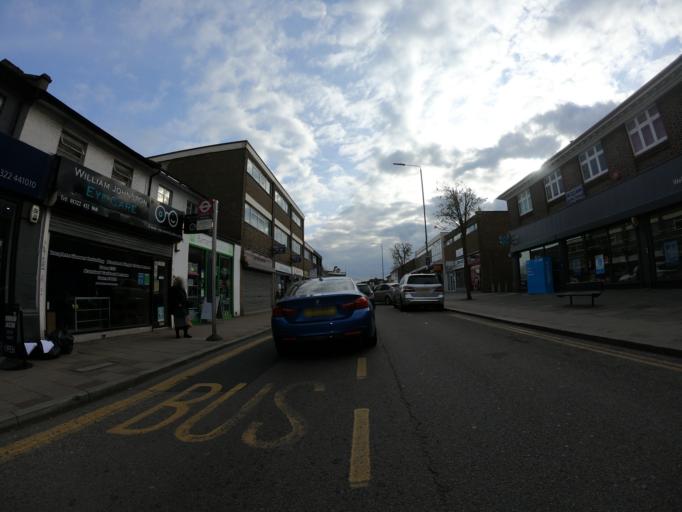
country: GB
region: England
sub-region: Greater London
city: Belvedere
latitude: 51.4819
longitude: 0.1454
